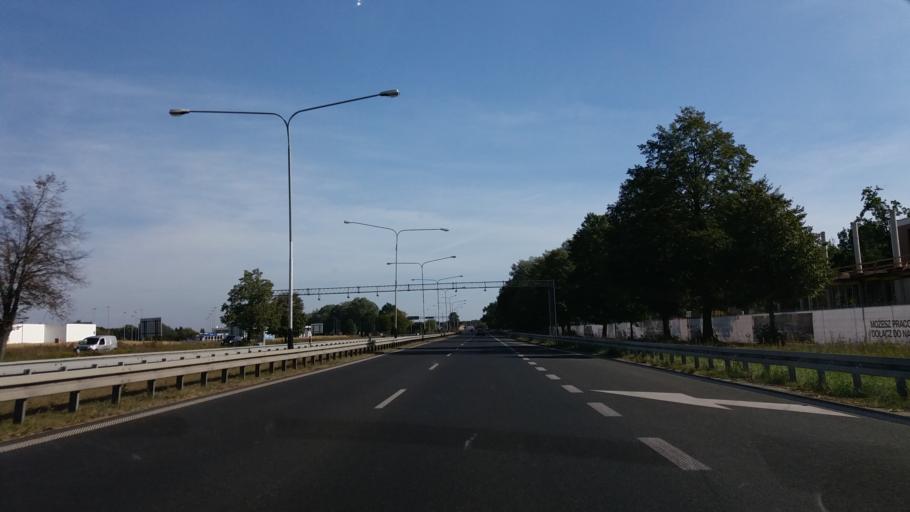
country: PL
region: Greater Poland Voivodeship
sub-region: Powiat poznanski
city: Baranowo
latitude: 52.4392
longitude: 16.7585
